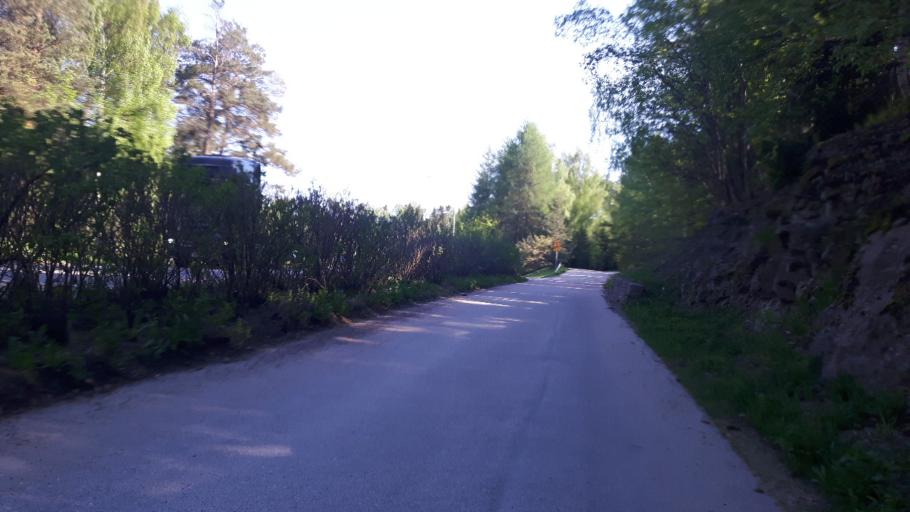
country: FI
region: Kymenlaakso
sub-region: Kotka-Hamina
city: Kotka
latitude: 60.4511
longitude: 26.8949
